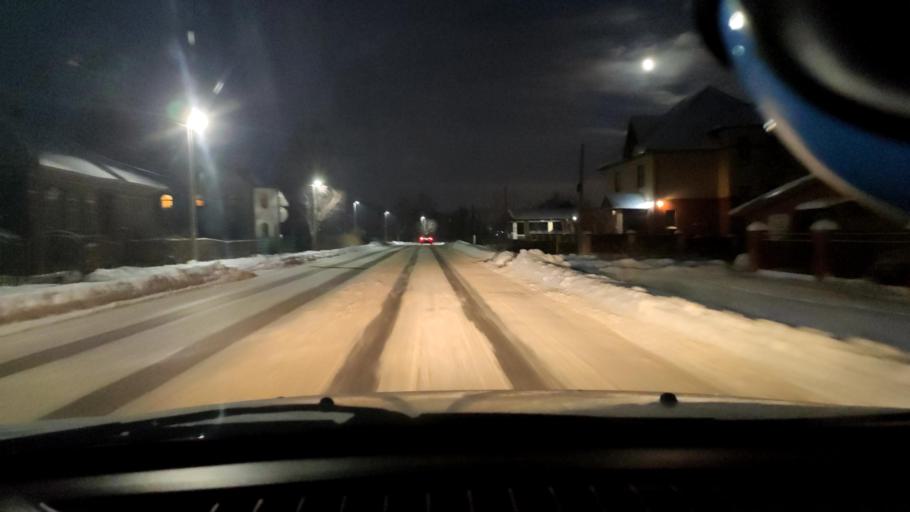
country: RU
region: Perm
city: Kultayevo
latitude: 57.8943
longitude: 55.9359
